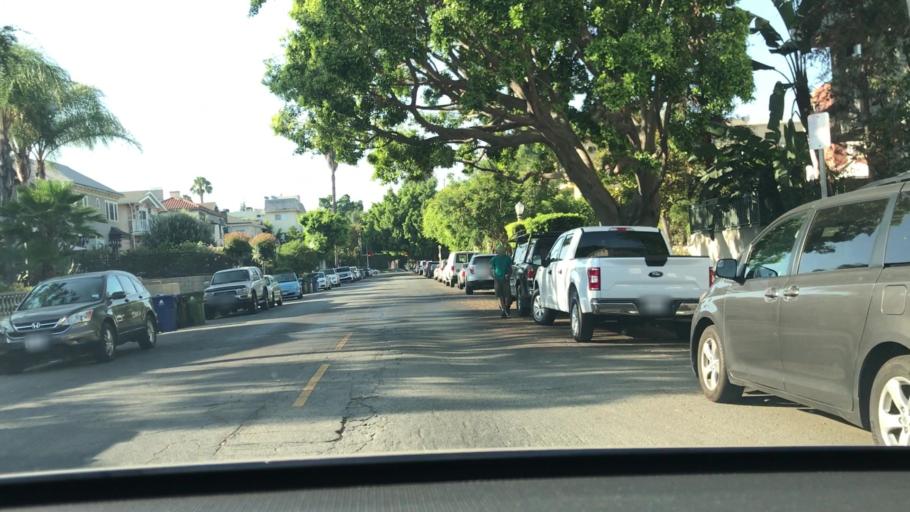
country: US
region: California
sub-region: Los Angeles County
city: Hollywood
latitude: 34.0672
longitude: -118.3173
